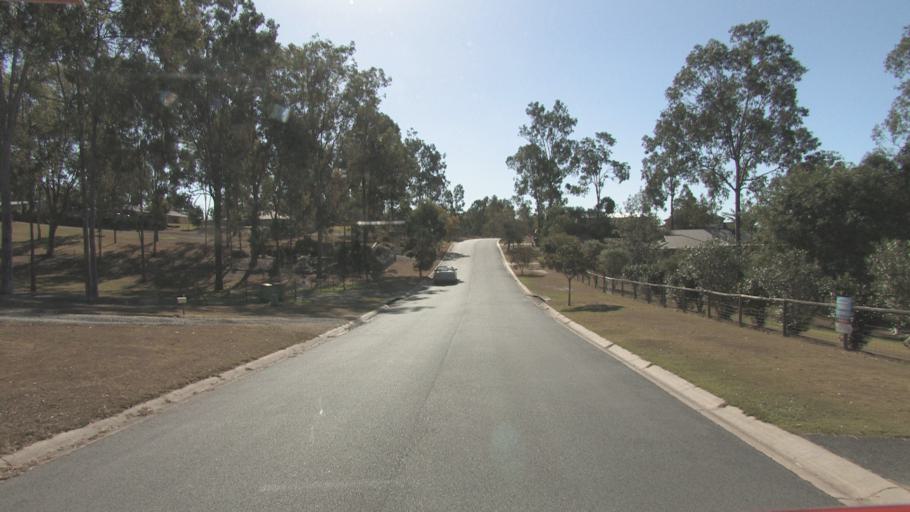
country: AU
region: Queensland
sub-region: Logan
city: Cedar Vale
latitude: -27.8669
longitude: 153.0361
